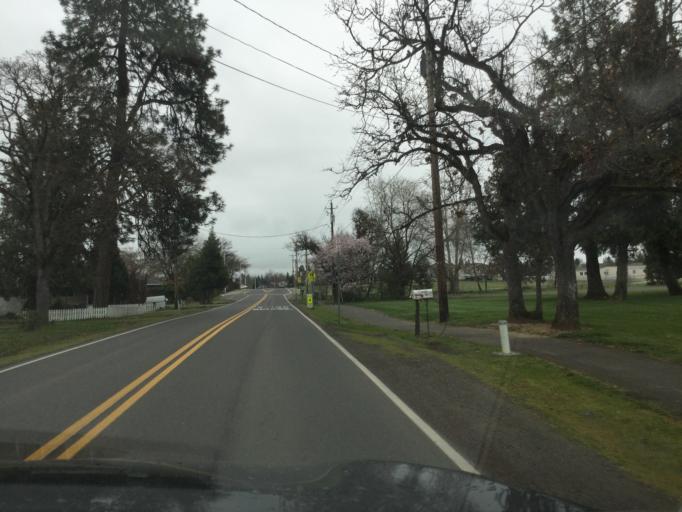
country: US
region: Oregon
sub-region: Jackson County
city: Central Point
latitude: 42.3885
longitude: -122.9238
